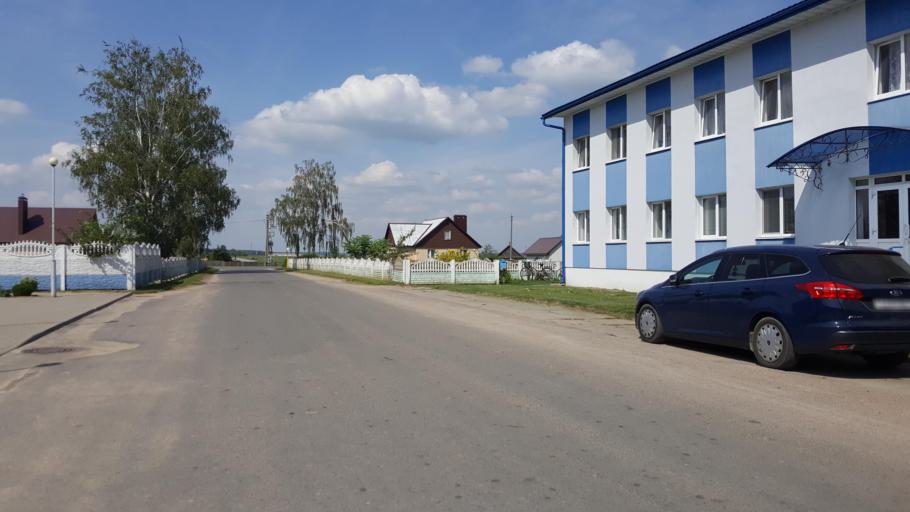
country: PL
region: Podlasie
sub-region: Powiat hajnowski
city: Czeremcha
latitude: 52.4981
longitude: 23.5690
